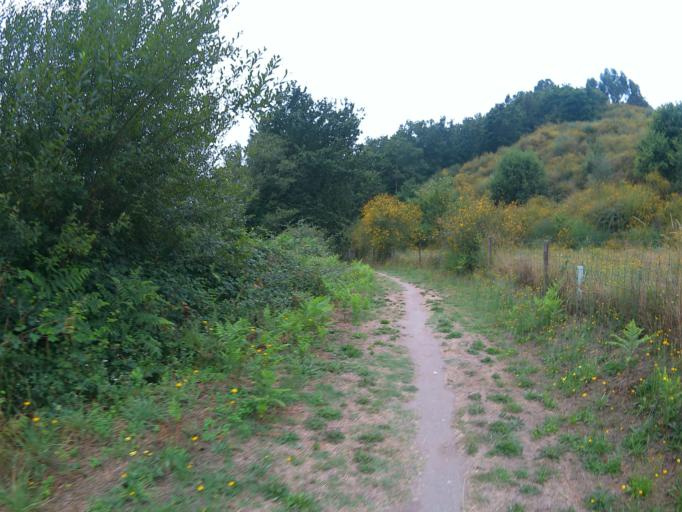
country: PT
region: Viana do Castelo
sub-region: Ponte da Barca
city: Ponte da Barca
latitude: 41.8048
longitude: -8.4555
